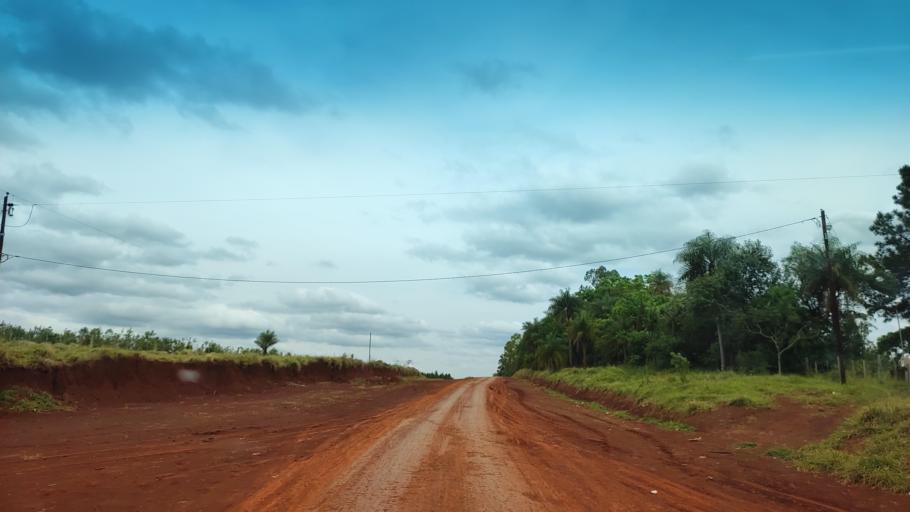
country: AR
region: Misiones
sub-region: Departamento de Capital
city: Posadas
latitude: -27.4846
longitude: -55.9708
